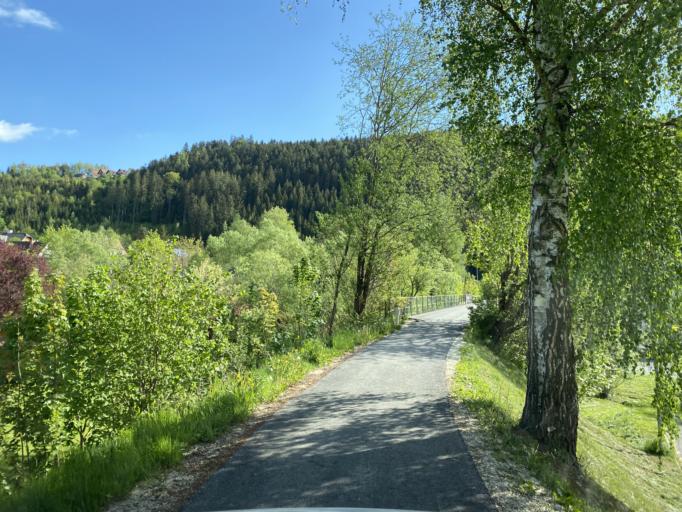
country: AT
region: Styria
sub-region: Politischer Bezirk Weiz
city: Birkfeld
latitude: 47.3552
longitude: 15.6993
